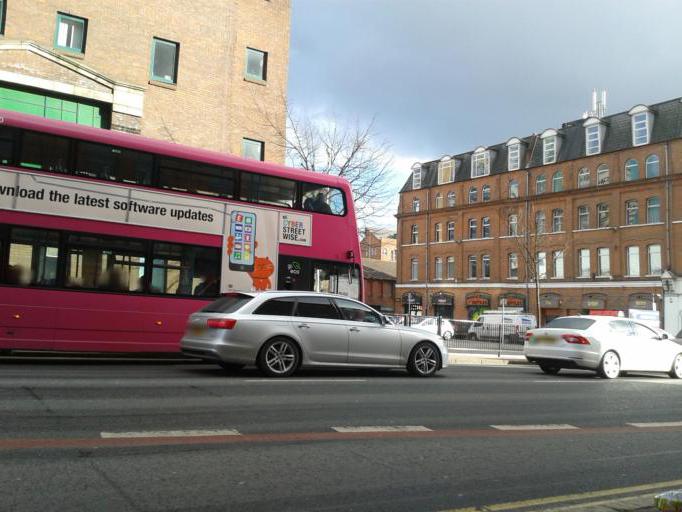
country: GB
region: Northern Ireland
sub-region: City of Belfast
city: Belfast
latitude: 54.5937
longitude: -5.9343
